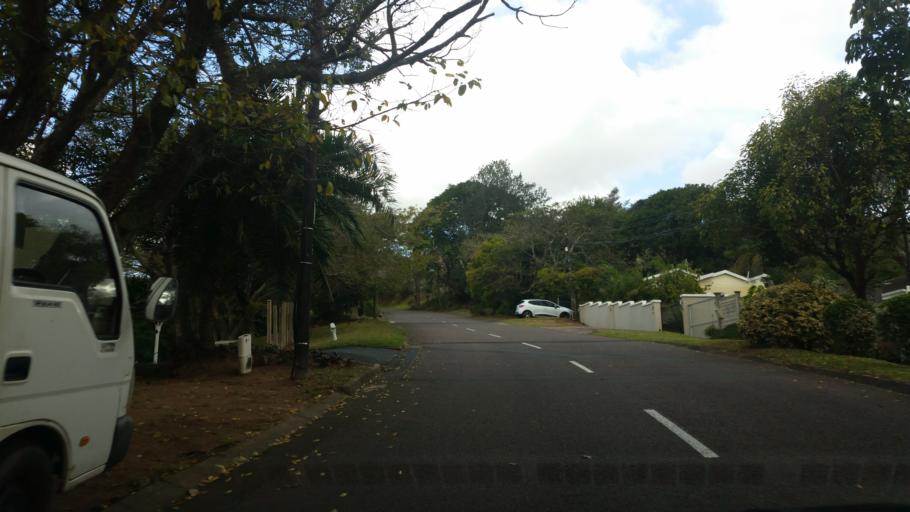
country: ZA
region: KwaZulu-Natal
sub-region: eThekwini Metropolitan Municipality
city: Berea
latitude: -29.8226
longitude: 30.9357
